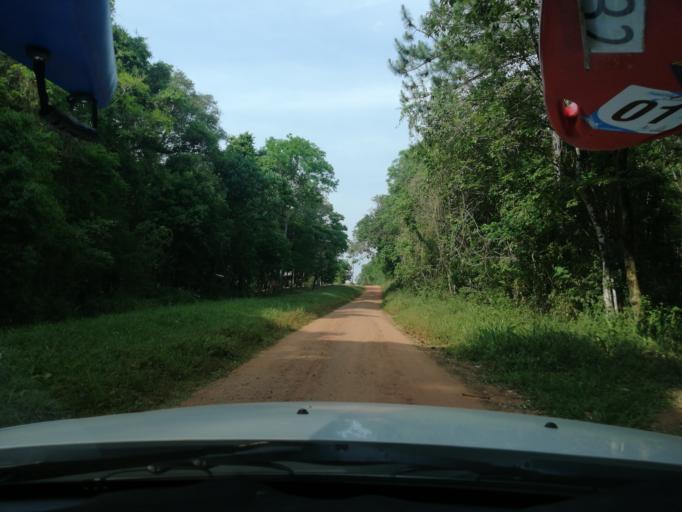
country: AR
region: Misiones
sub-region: Departamento de San Ignacio
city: San Ignacio
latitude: -27.2988
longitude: -55.5738
